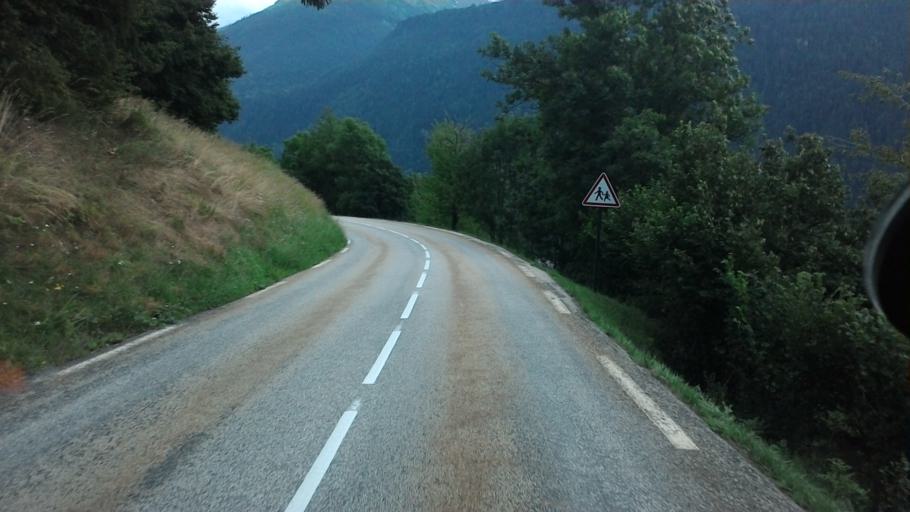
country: FR
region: Rhone-Alpes
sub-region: Departement de la Savoie
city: Seez
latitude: 45.6239
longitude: 6.8176
